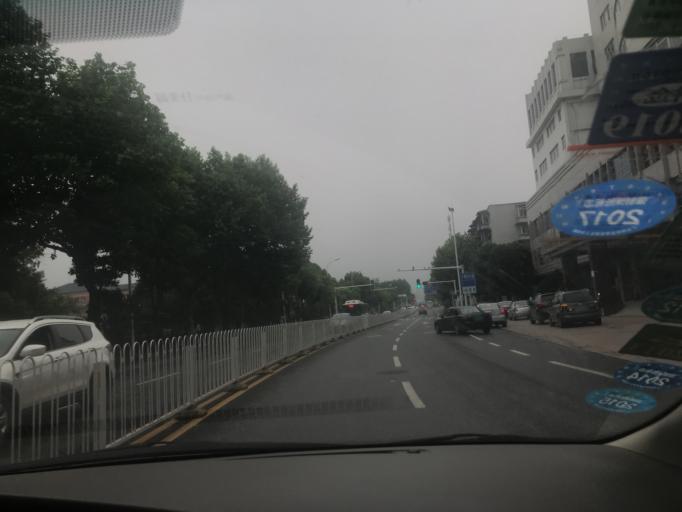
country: CN
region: Hubei
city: Wuhan
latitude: 30.5522
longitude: 114.2719
